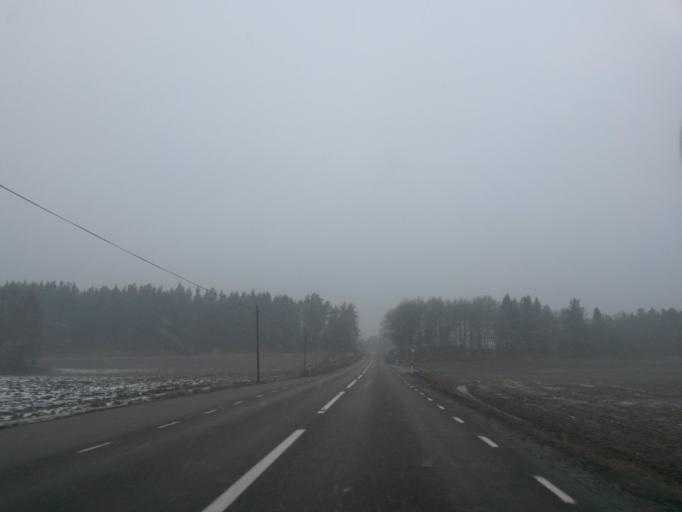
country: SE
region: Vaestra Goetaland
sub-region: Alingsas Kommun
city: Sollebrunn
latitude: 58.2087
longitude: 12.4336
